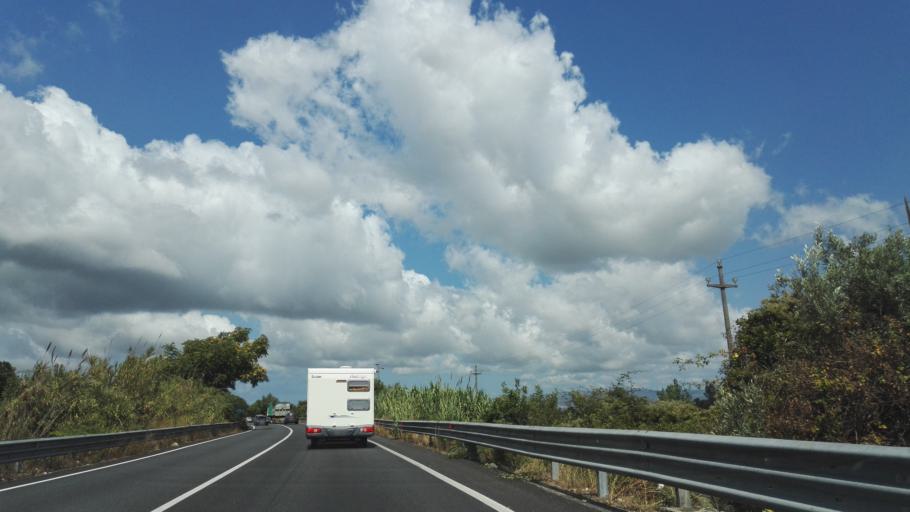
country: IT
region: Calabria
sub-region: Provincia di Reggio Calabria
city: Melicucco
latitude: 38.4506
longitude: 16.0334
